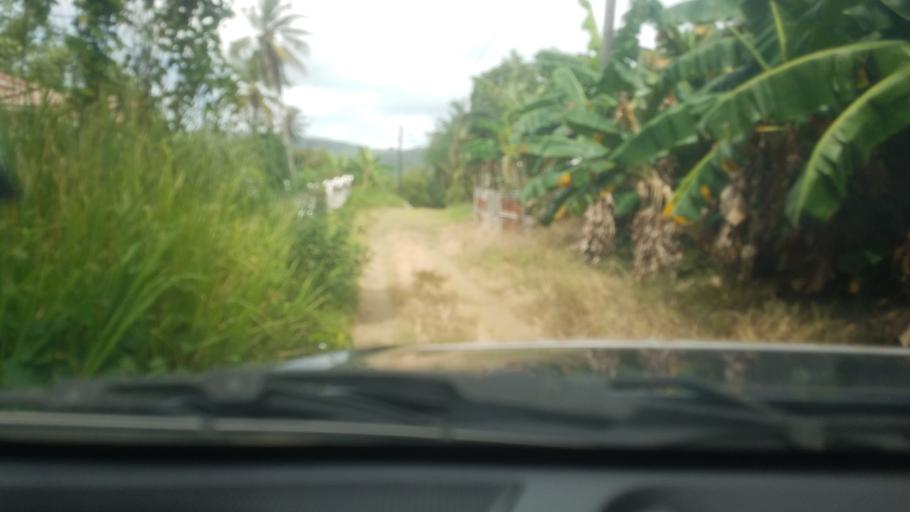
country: LC
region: Micoud Quarter
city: Micoud
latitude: 13.7966
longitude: -60.9307
